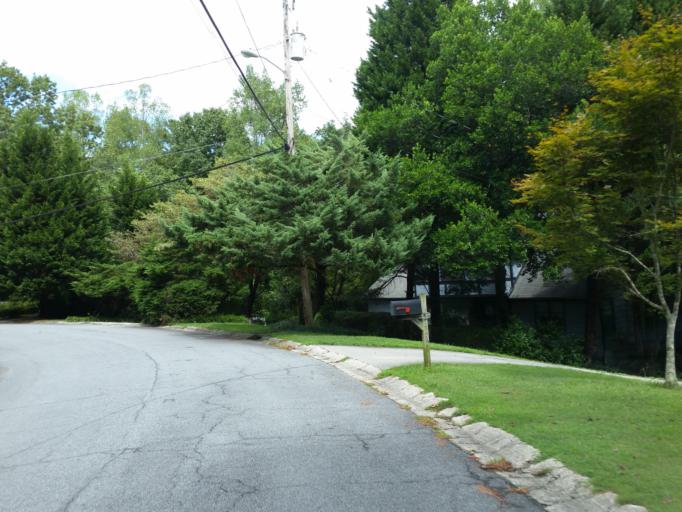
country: US
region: Georgia
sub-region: Cobb County
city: Smyrna
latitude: 33.9480
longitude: -84.4726
